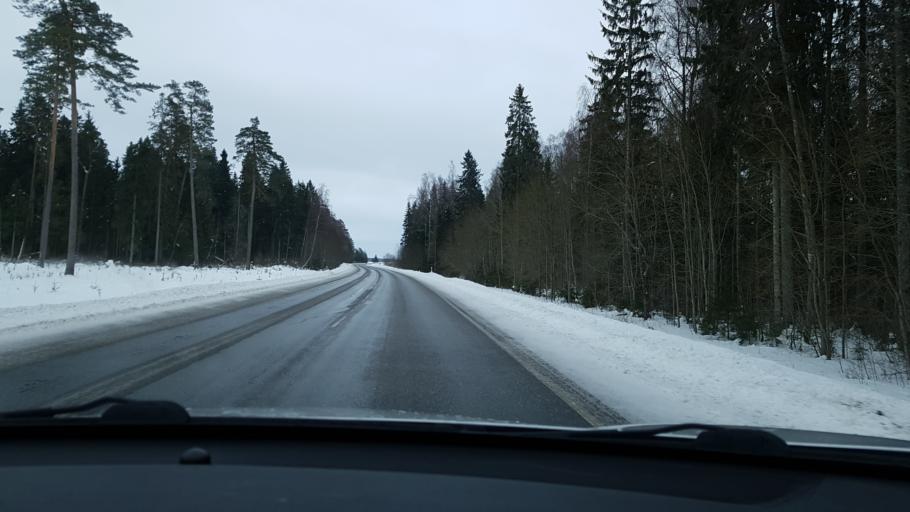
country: EE
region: Jaervamaa
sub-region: Jaerva-Jaani vald
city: Jarva-Jaani
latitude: 59.0961
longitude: 25.8218
